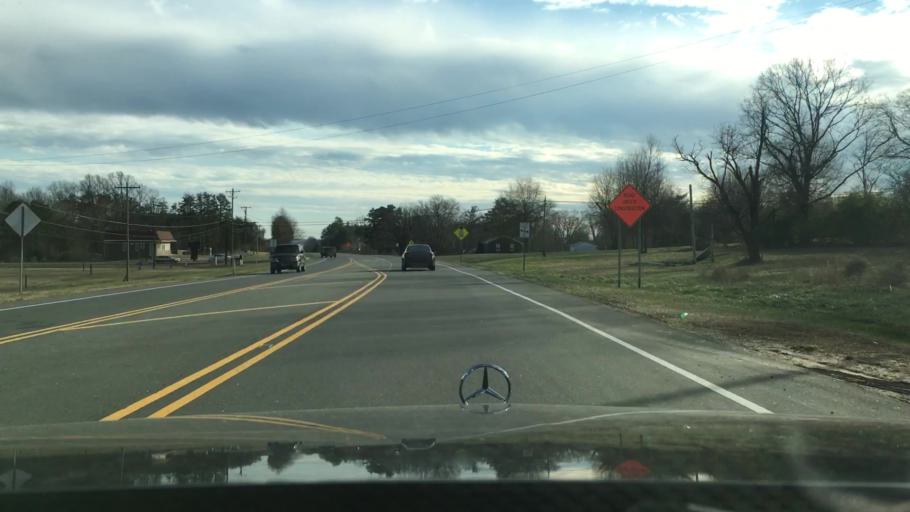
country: US
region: Virginia
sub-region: City of Danville
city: Danville
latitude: 36.5330
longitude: -79.3998
